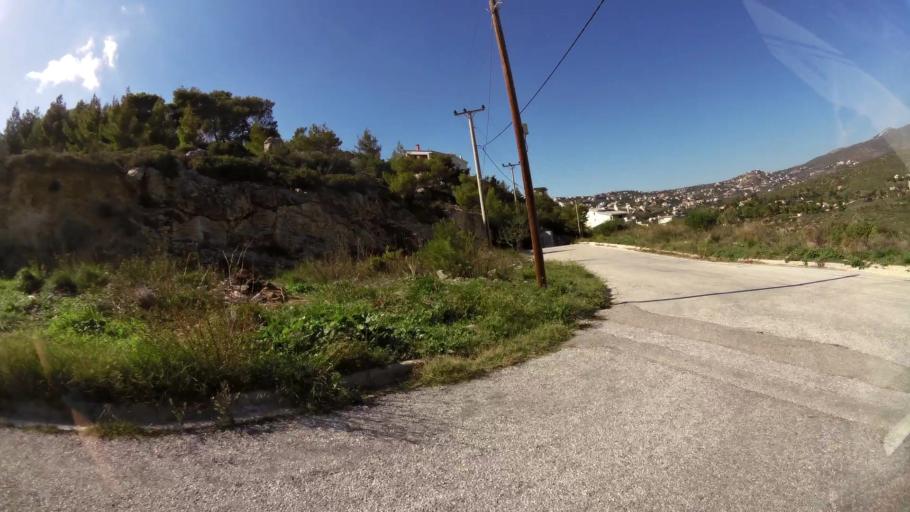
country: GR
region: Attica
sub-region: Nomarchia Anatolikis Attikis
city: Dioni
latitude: 38.0199
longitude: 23.9221
